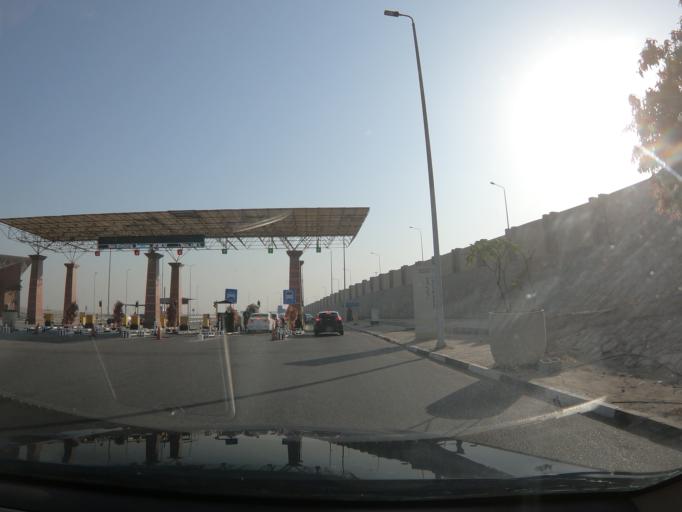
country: EG
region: Muhafazat al Qalyubiyah
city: Al Khankah
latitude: 30.1090
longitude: 31.3858
